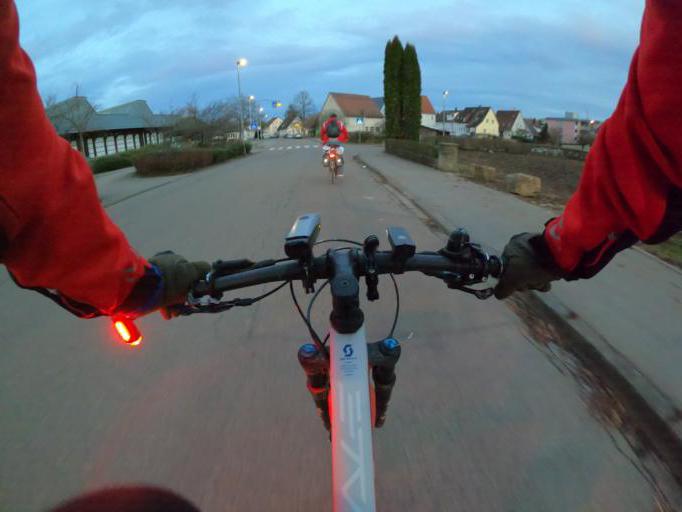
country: DE
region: Baden-Wuerttemberg
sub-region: Regierungsbezirk Stuttgart
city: Reichenbach an der Fils
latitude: 48.7106
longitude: 9.4558
